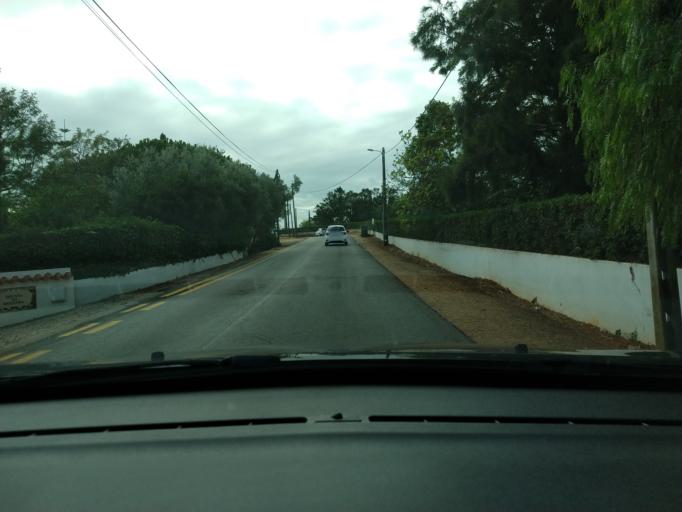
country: PT
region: Faro
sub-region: Lagoa
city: Carvoeiro
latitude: 37.0951
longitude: -8.4165
